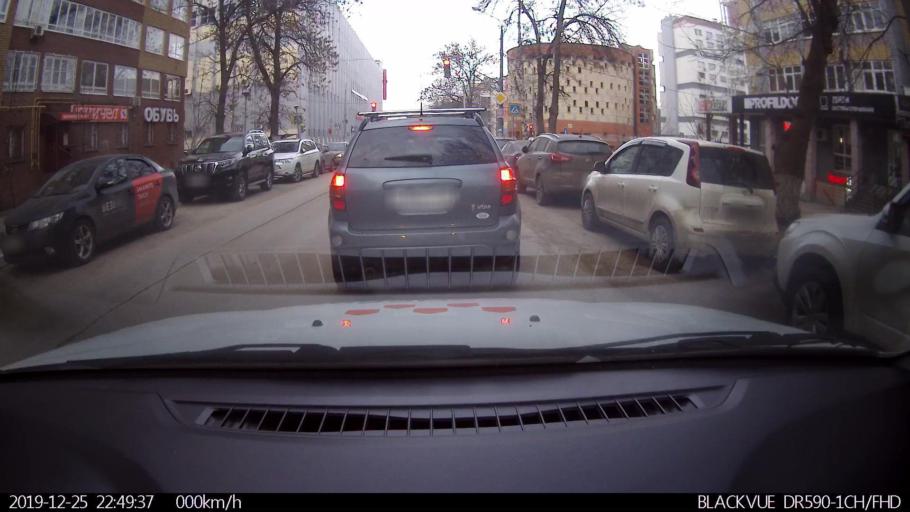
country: RU
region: Nizjnij Novgorod
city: Nizhniy Novgorod
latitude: 56.3152
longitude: 44.0212
